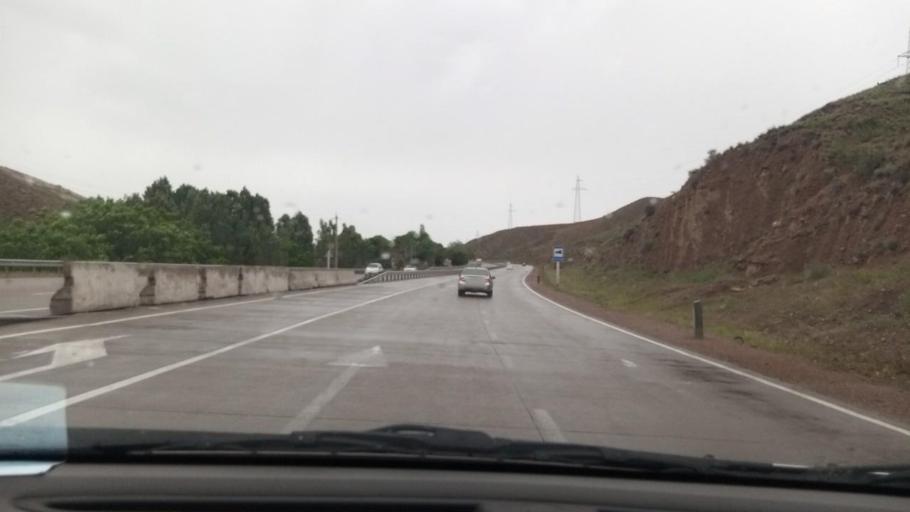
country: UZ
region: Namangan
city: Pop Shahri
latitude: 40.9492
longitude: 70.6800
